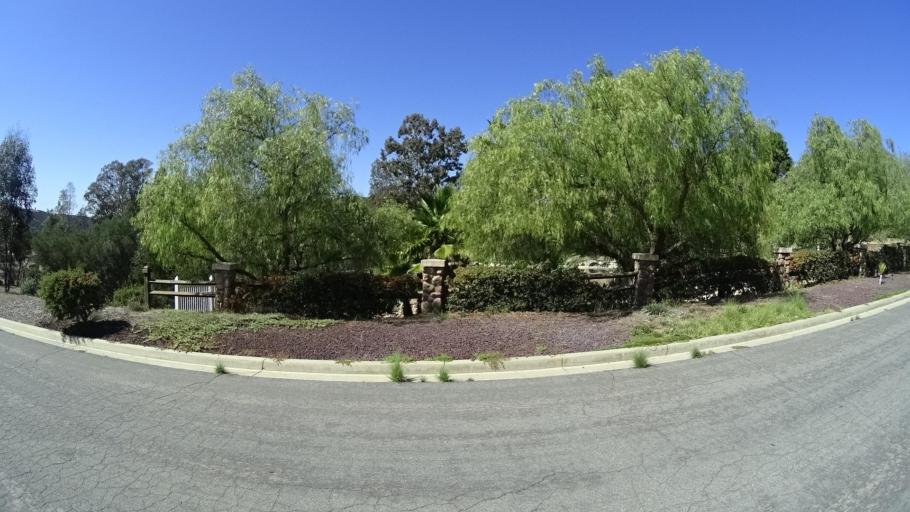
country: US
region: California
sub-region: San Diego County
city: Alpine
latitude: 32.8073
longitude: -116.7790
